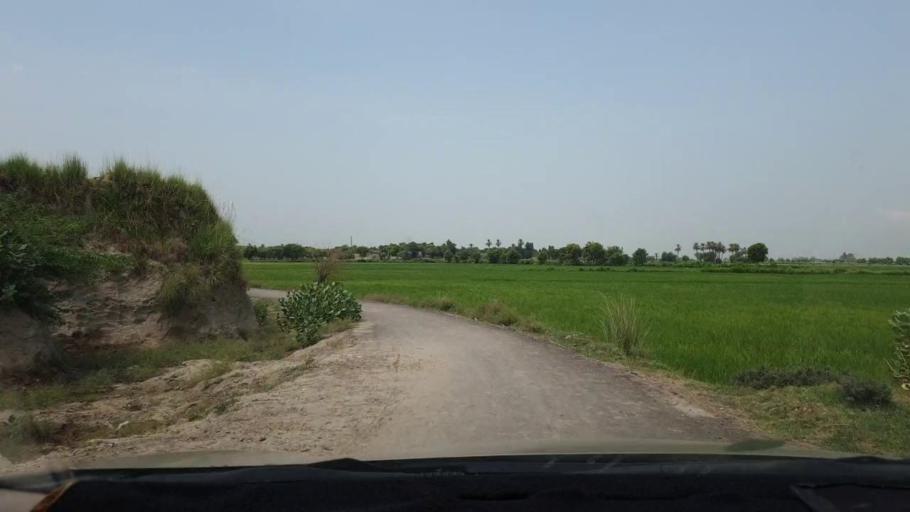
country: PK
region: Sindh
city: Naudero
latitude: 27.6567
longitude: 68.3306
